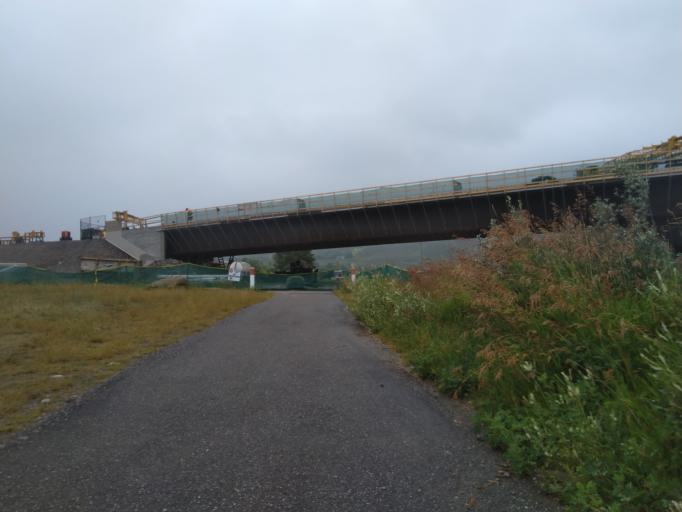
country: CA
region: Alberta
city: Cochrane
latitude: 51.1753
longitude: -114.4472
